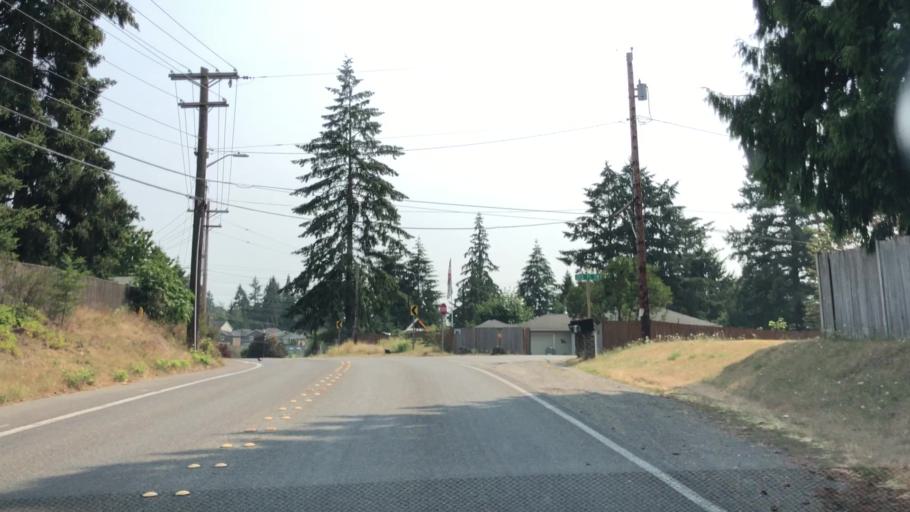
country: US
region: Washington
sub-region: Snohomish County
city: Brier
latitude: 47.8056
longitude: -122.2535
